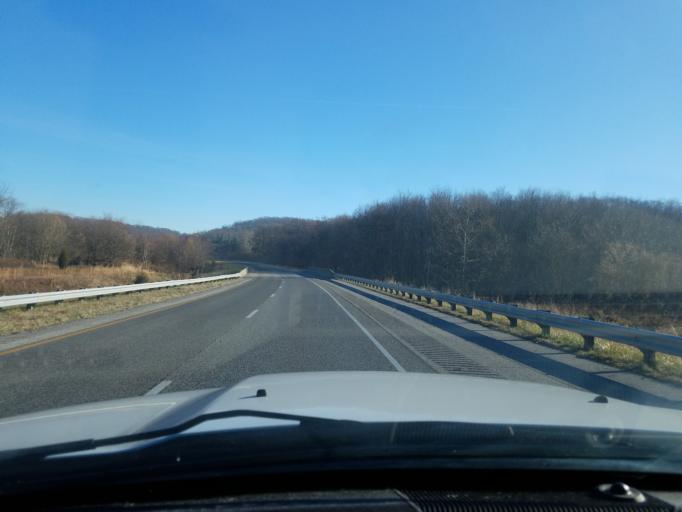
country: US
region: Indiana
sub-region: Dubois County
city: Ferdinand
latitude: 38.2057
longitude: -86.7835
